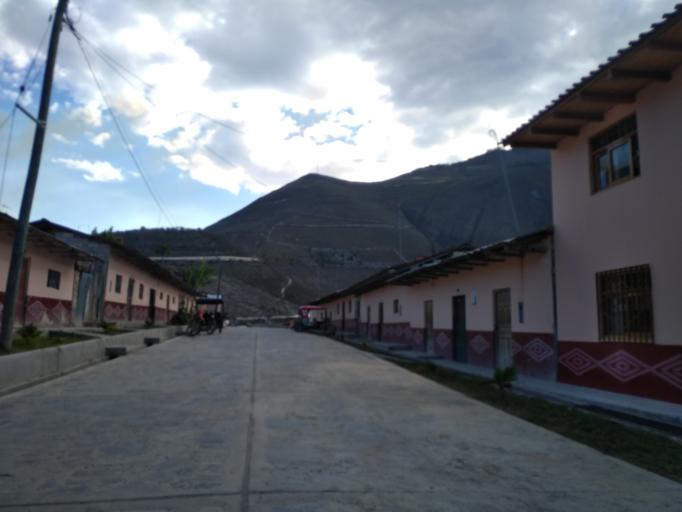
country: PE
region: Amazonas
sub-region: Provincia de Luya
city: Tingo
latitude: -6.3720
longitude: -77.9105
